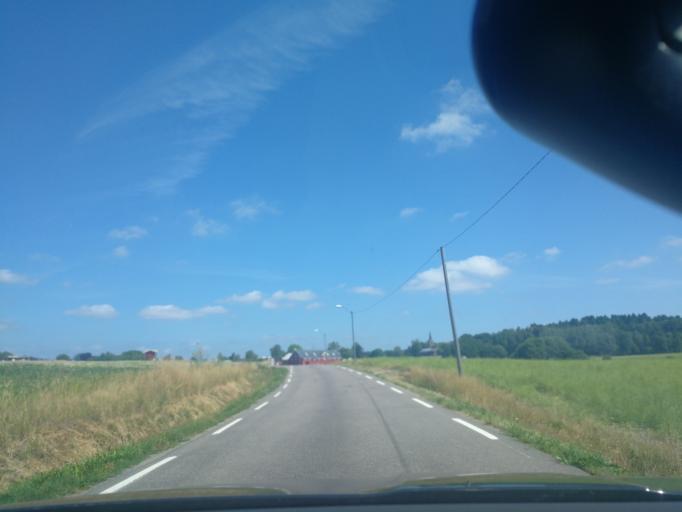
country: NO
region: Vestfold
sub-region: Stokke
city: Stokke
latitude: 59.2136
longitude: 10.2946
